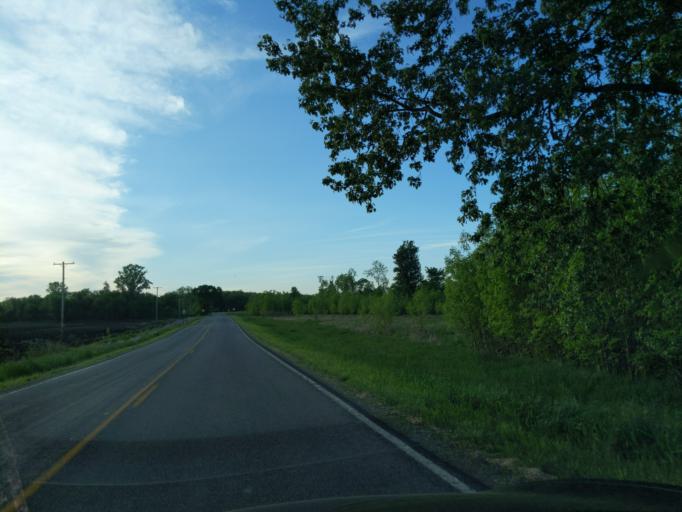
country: US
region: Michigan
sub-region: Ingham County
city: Leslie
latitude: 42.4639
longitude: -84.3150
